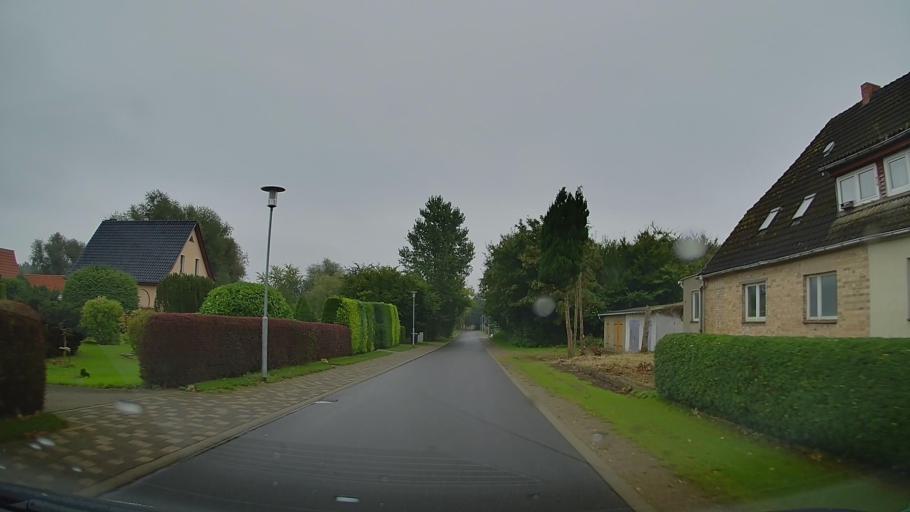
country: DE
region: Mecklenburg-Vorpommern
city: Klutz
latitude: 53.9934
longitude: 11.1255
